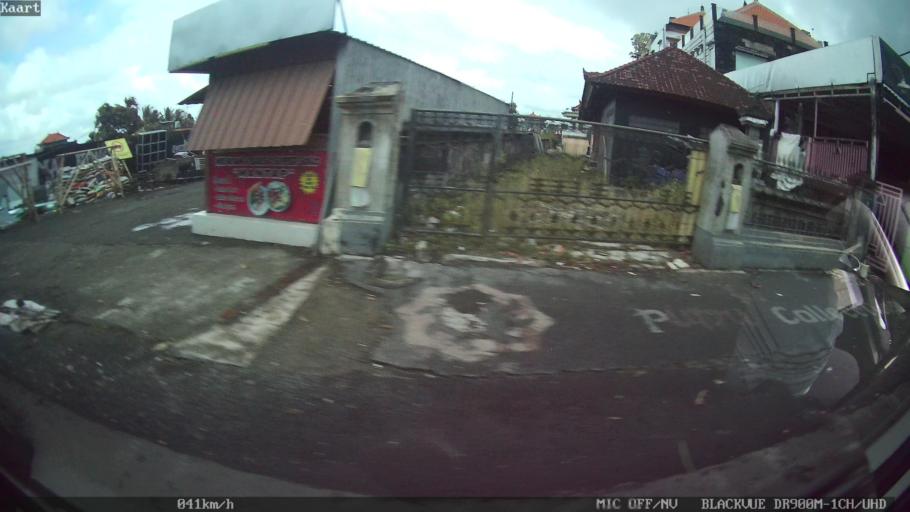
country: ID
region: Bali
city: Banjar Keraman
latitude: -8.5387
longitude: 115.2143
